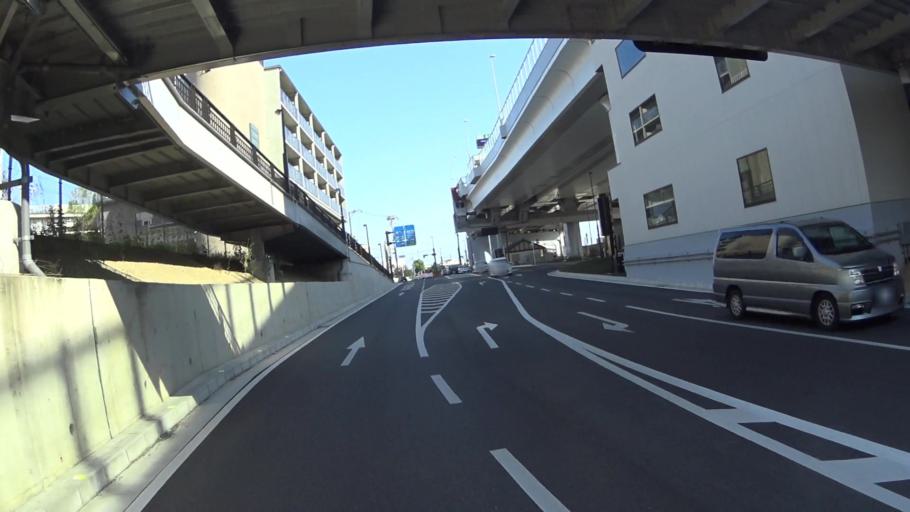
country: JP
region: Kyoto
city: Yawata
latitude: 34.9136
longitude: 135.6886
